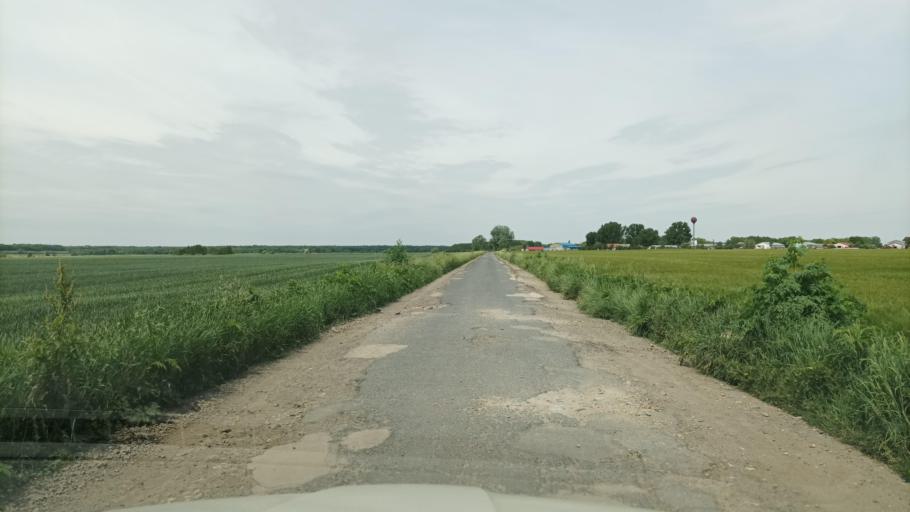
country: HU
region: Fejer
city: Racalmas
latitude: 47.0725
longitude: 18.9523
